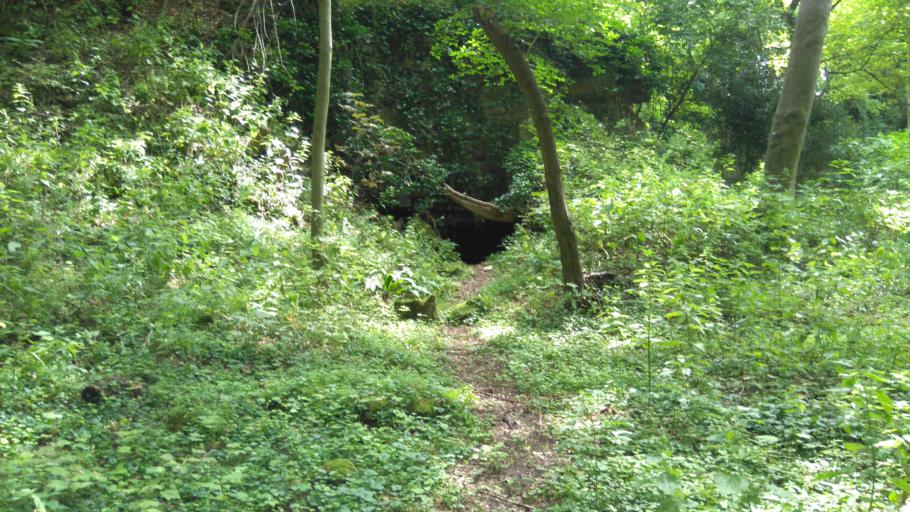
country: FR
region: Picardie
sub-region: Departement de l'Oise
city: Saint-Maximin
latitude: 49.2381
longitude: 2.4505
